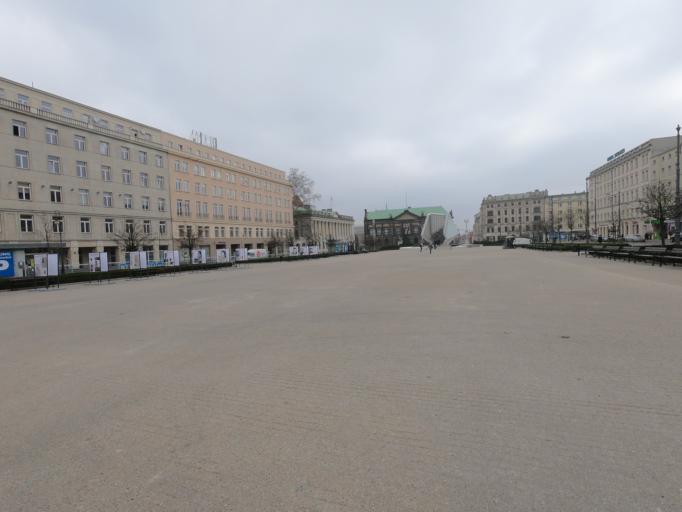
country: PL
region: Greater Poland Voivodeship
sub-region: Poznan
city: Poznan
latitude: 52.4081
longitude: 16.9268
